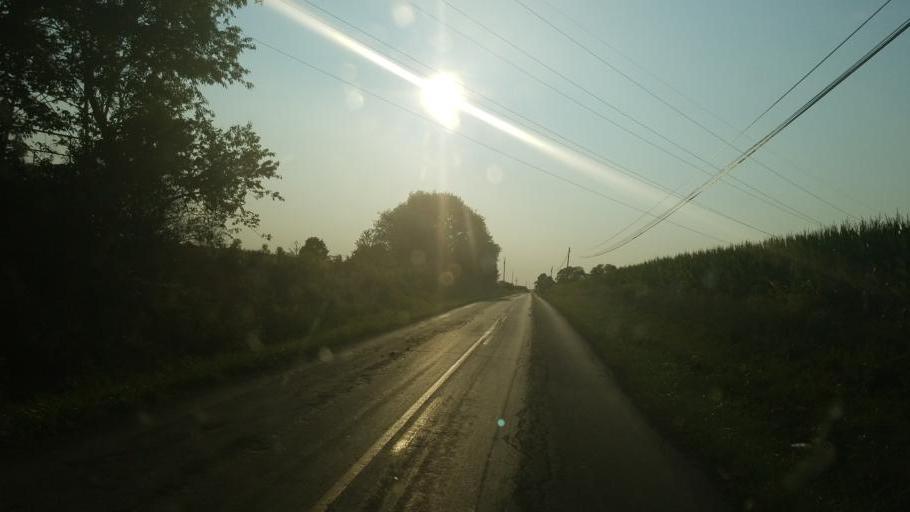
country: US
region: Ohio
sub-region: Wayne County
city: Apple Creek
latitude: 40.6743
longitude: -81.8890
